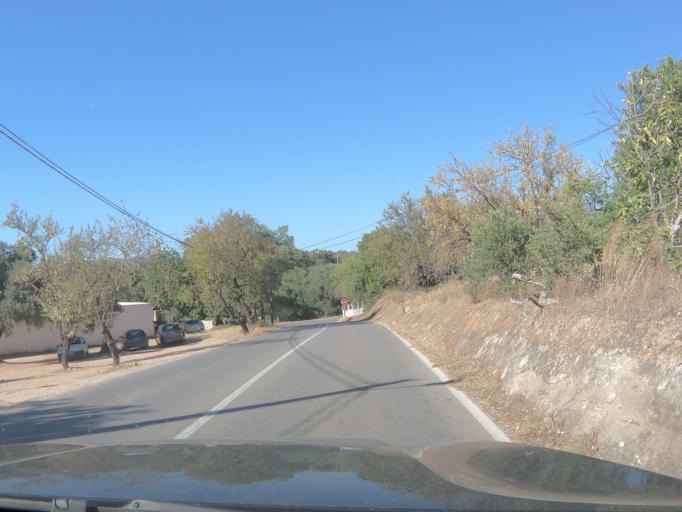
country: PT
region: Faro
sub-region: Loule
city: Almancil
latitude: 37.1079
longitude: -8.0415
